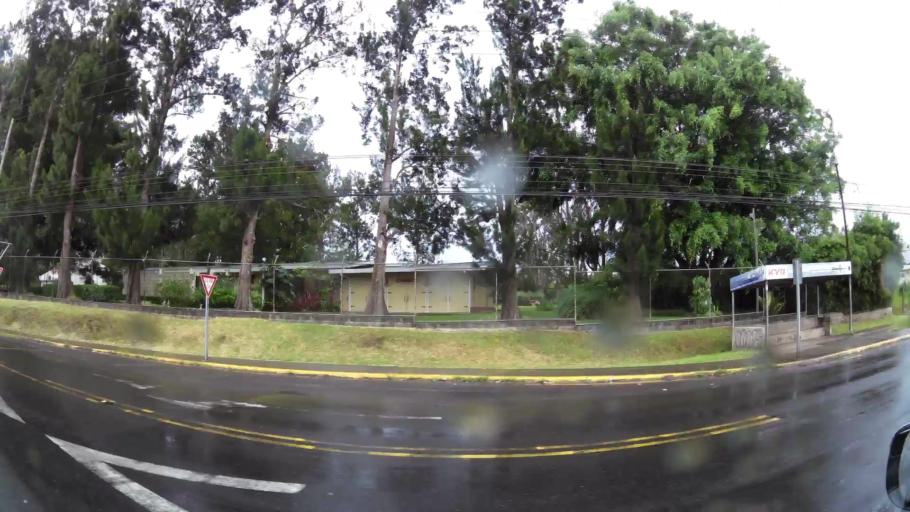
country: CR
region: Cartago
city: Cartago
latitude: 9.8484
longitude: -83.8964
